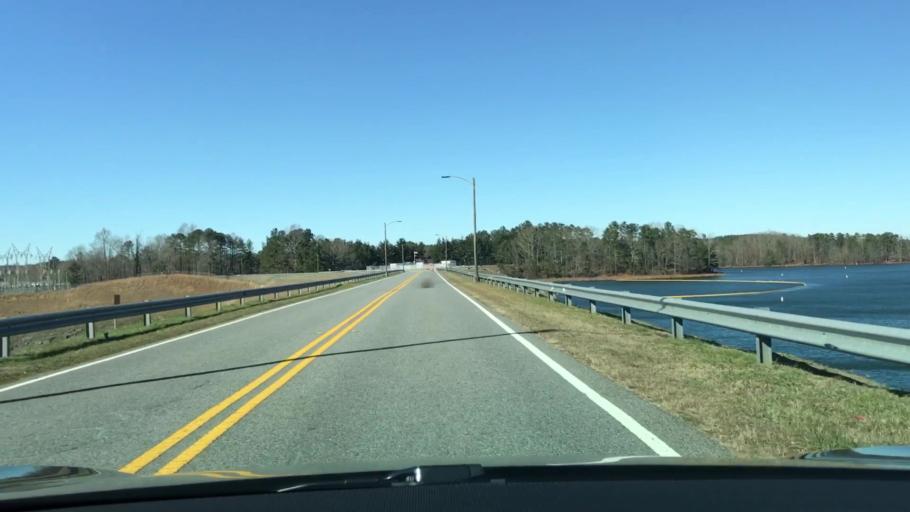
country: US
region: Georgia
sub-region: Gwinnett County
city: Sugar Hill
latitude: 34.1601
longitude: -84.0736
